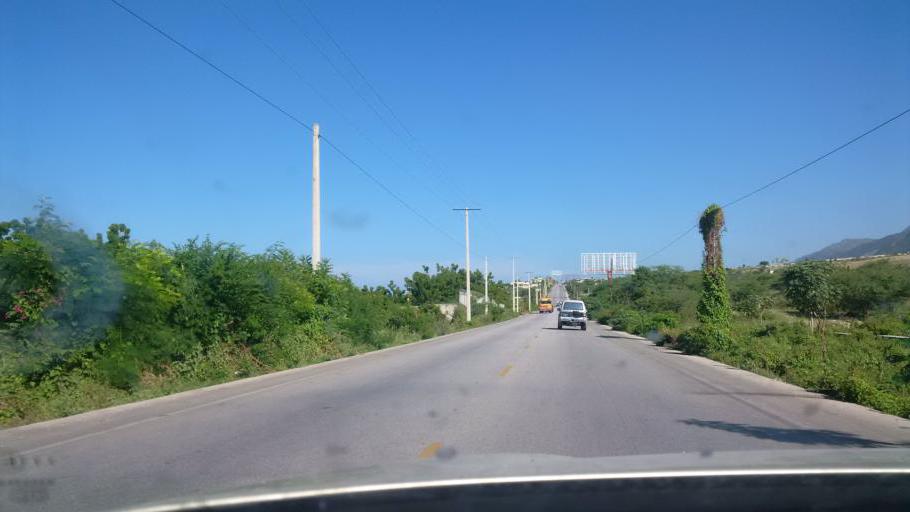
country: HT
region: Ouest
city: Cabaret
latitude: 18.8337
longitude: -72.5615
